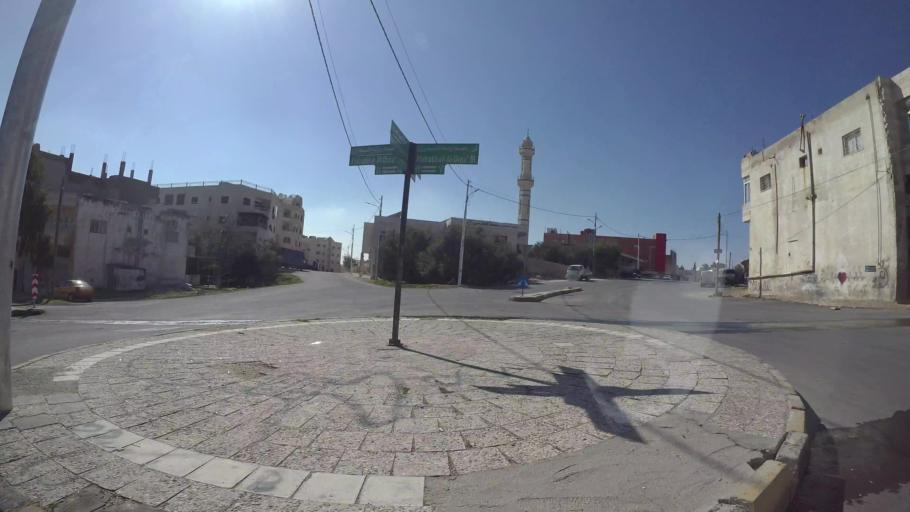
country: JO
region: Amman
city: Al Bunayyat ash Shamaliyah
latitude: 31.9070
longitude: 35.8995
